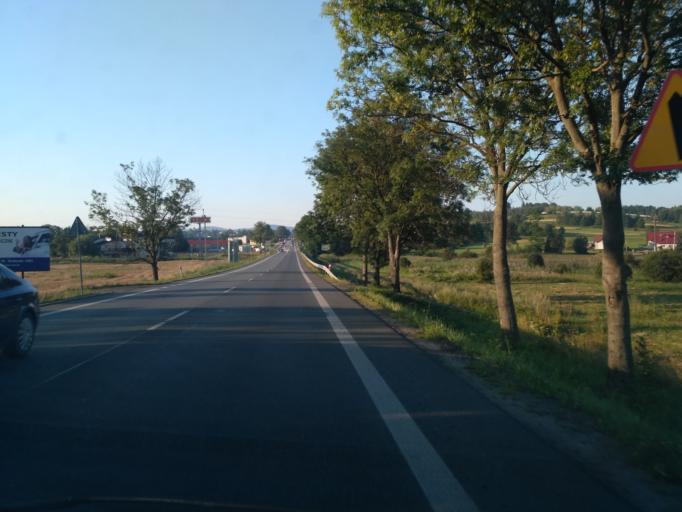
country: PL
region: Subcarpathian Voivodeship
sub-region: Powiat krosnienski
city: Miejsce Piastowe
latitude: 49.6484
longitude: 21.7829
